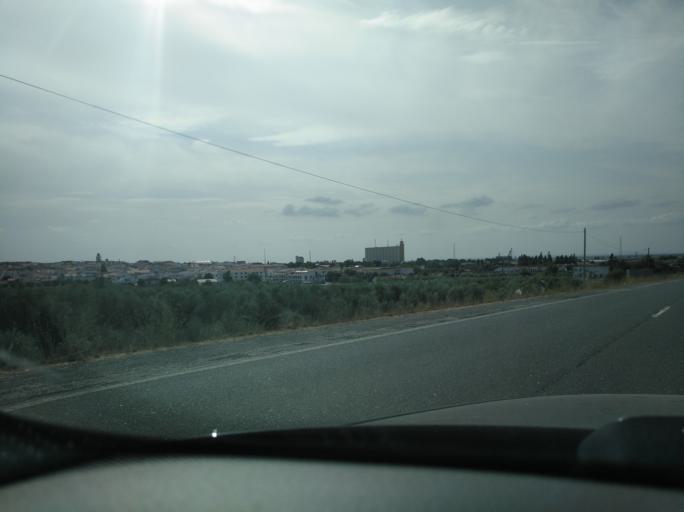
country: PT
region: Beja
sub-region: Beja
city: Ferreira do Alentejo
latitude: 38.0636
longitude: -8.1088
